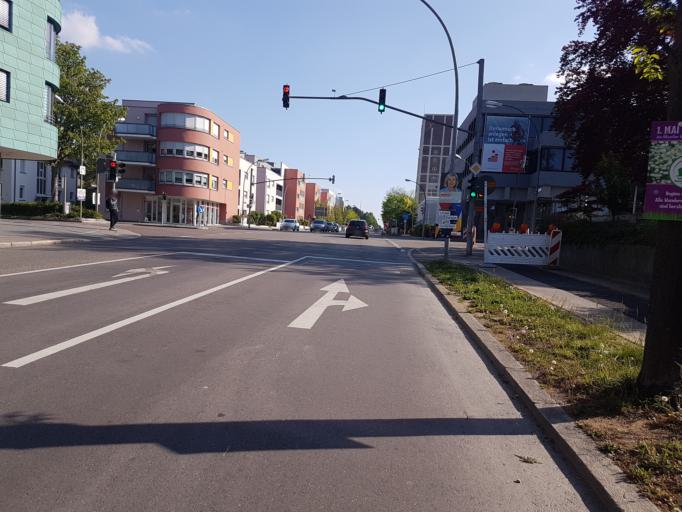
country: DE
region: Baden-Wuerttemberg
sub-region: Regierungsbezirk Stuttgart
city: Kornwestheim
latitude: 48.8619
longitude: 9.1857
